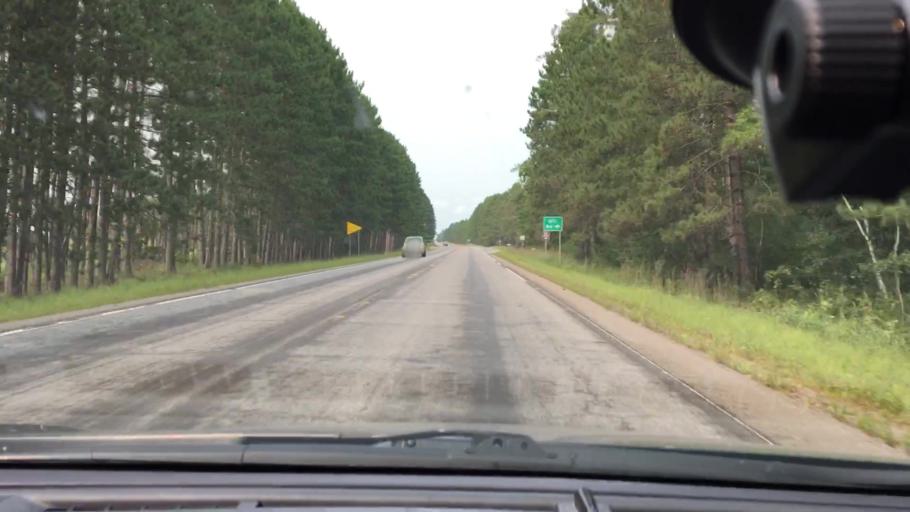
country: US
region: Minnesota
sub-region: Crow Wing County
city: Cross Lake
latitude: 46.7577
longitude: -93.9666
